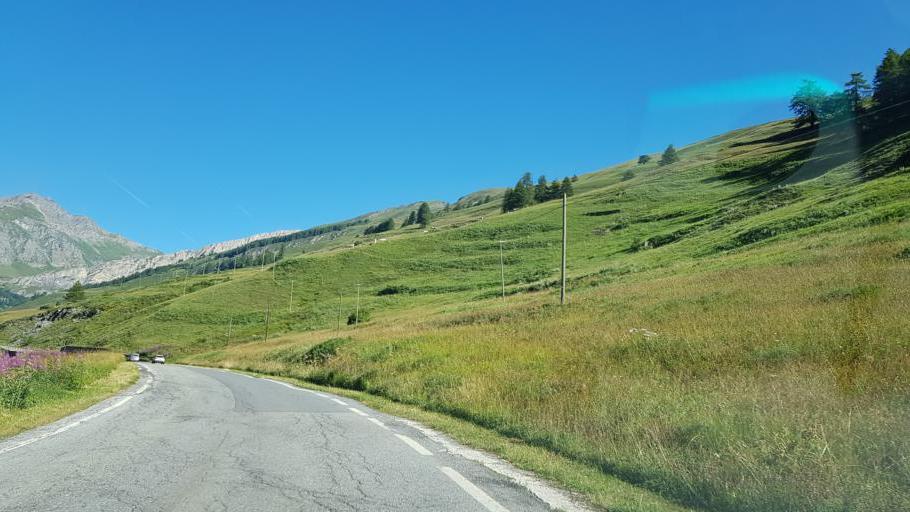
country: IT
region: Piedmont
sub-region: Provincia di Cuneo
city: Pontechianale
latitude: 44.6328
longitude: 7.0171
